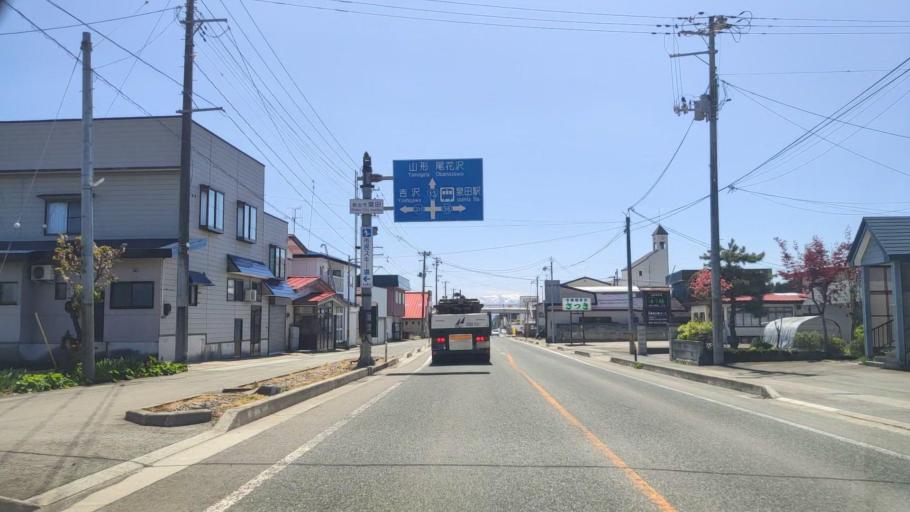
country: JP
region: Yamagata
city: Shinjo
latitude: 38.8124
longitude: 140.3237
